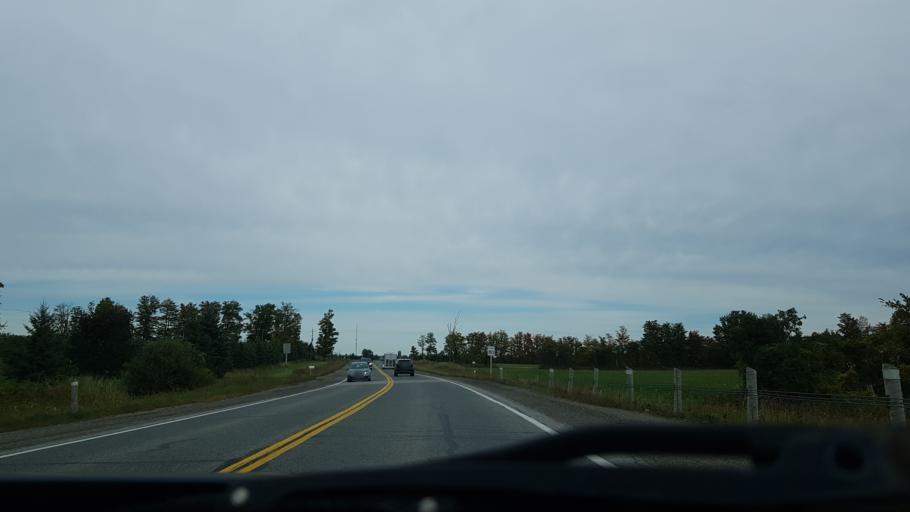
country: CA
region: Ontario
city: Orangeville
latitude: 43.8936
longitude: -79.9583
